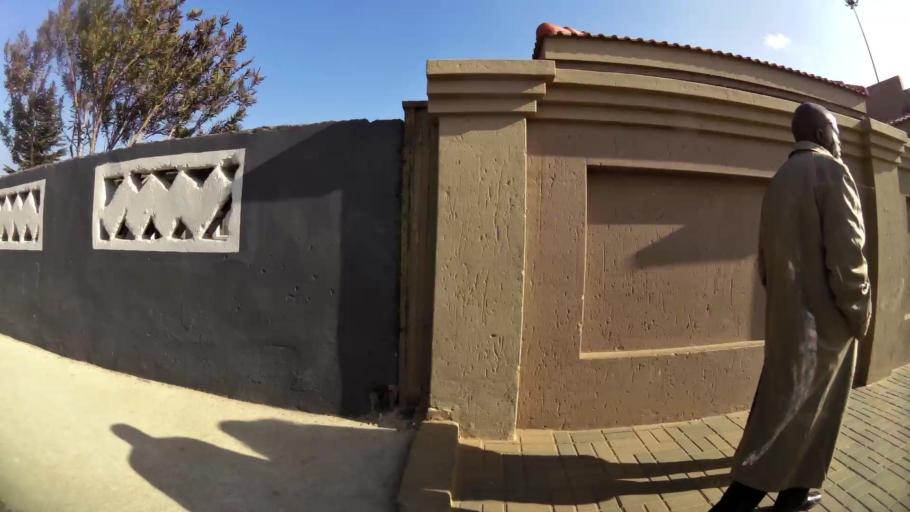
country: ZA
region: Gauteng
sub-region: City of Johannesburg Metropolitan Municipality
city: Soweto
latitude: -26.2573
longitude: 27.9154
